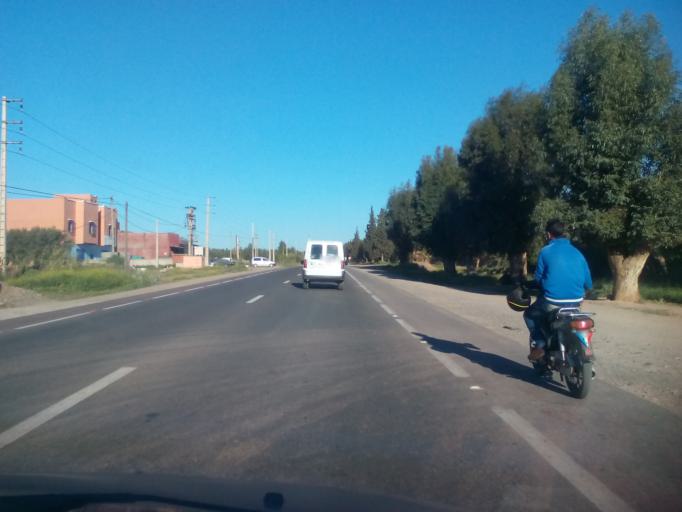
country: MA
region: Marrakech-Tensift-Al Haouz
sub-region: Marrakech
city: Marrakesh
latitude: 31.6317
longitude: -8.1889
